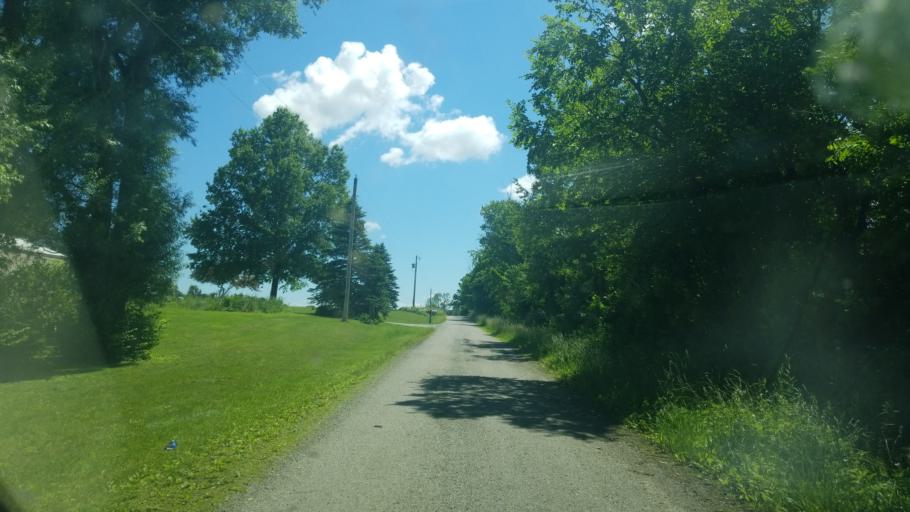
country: US
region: Ohio
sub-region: Huron County
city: New London
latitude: 41.1505
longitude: -82.3934
